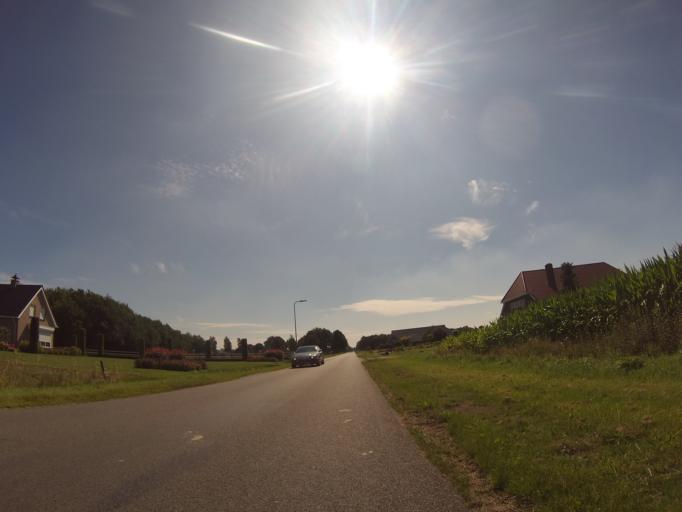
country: NL
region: Drenthe
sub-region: Gemeente Emmen
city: Schoonebeek
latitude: 52.6964
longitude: 6.9311
